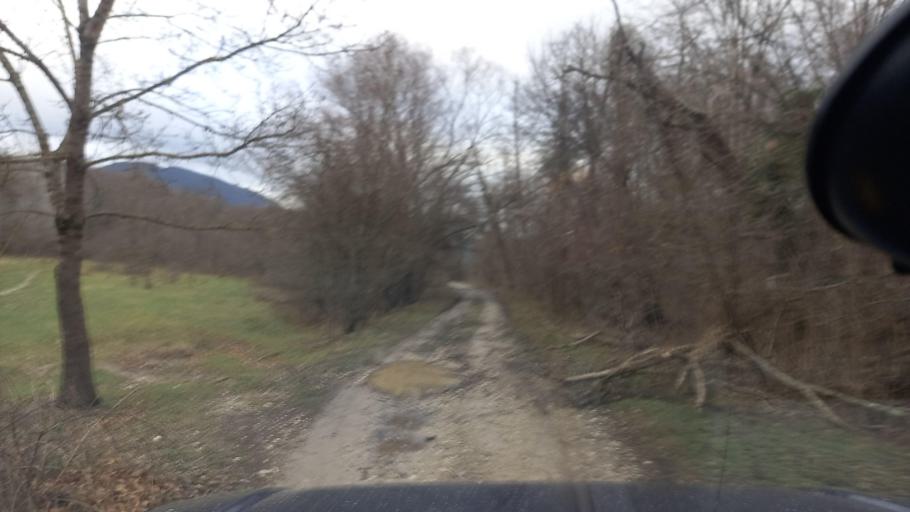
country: RU
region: Krasnodarskiy
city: Pshada
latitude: 44.4838
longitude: 38.4039
